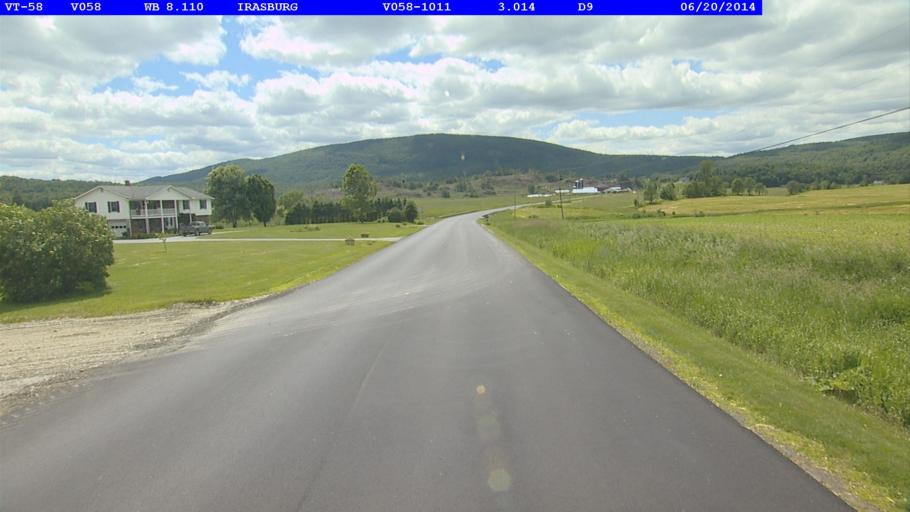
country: US
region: Vermont
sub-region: Orleans County
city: Newport
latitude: 44.8149
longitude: -72.2994
